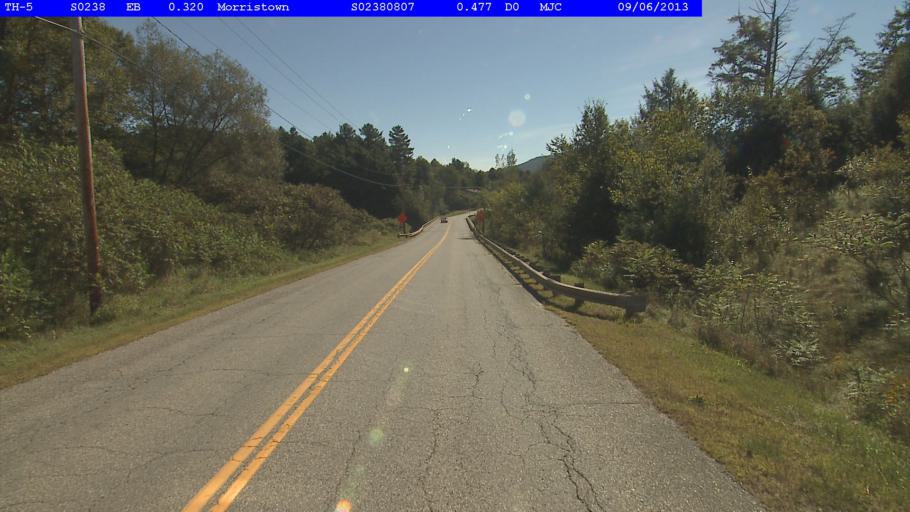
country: US
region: Vermont
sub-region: Lamoille County
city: Morrisville
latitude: 44.5656
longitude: -72.6092
